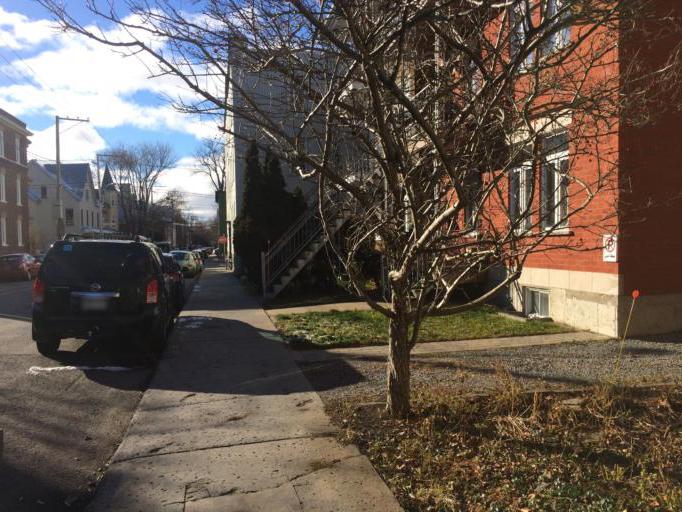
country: CA
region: Quebec
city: Quebec
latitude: 46.8031
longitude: -71.2271
